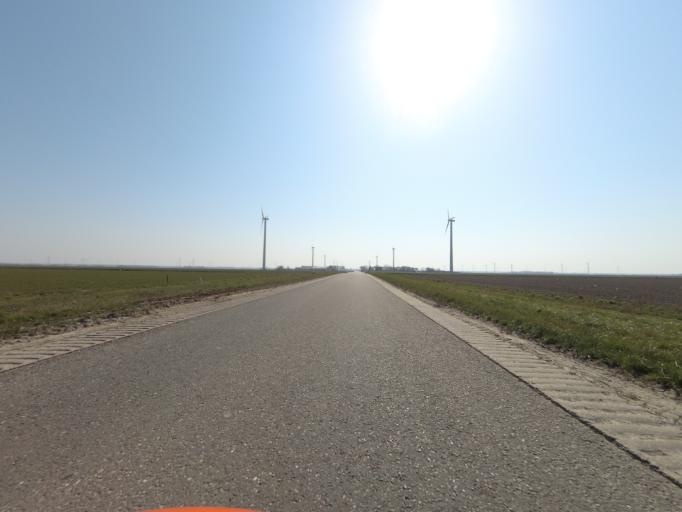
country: NL
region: Utrecht
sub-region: Gemeente Bunschoten
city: Spakenburg
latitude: 52.3489
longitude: 5.3694
